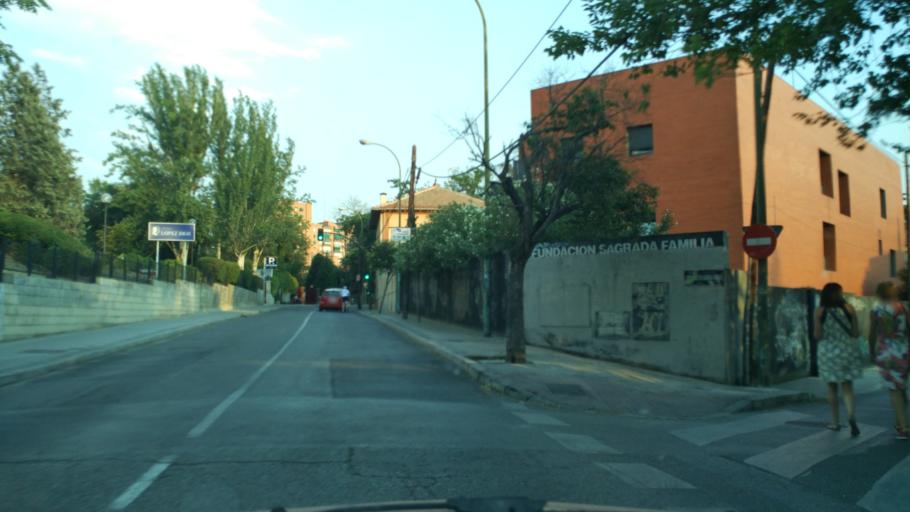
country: ES
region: Madrid
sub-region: Provincia de Madrid
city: Tetuan de las Victorias
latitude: 40.4685
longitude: -3.7251
